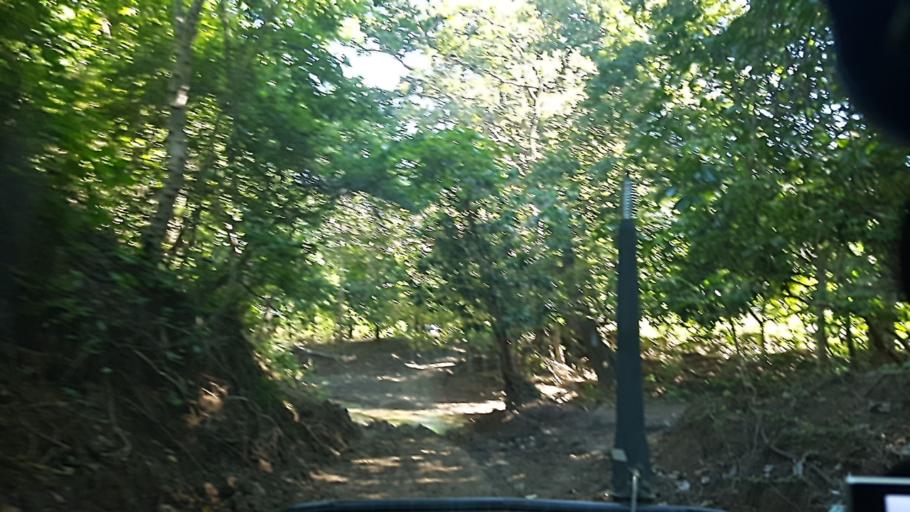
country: NI
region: Rivas
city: Tola
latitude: 11.5453
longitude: -86.0979
